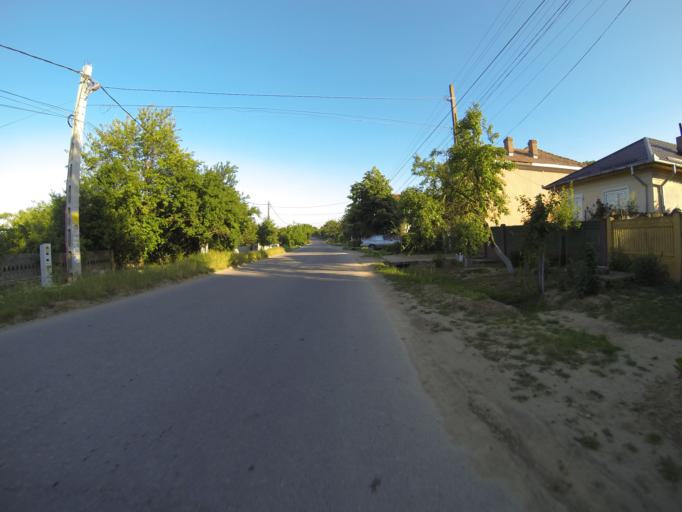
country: RO
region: Dolj
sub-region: Comuna Tuglui
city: Tuglui
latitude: 44.2103
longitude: 23.7940
